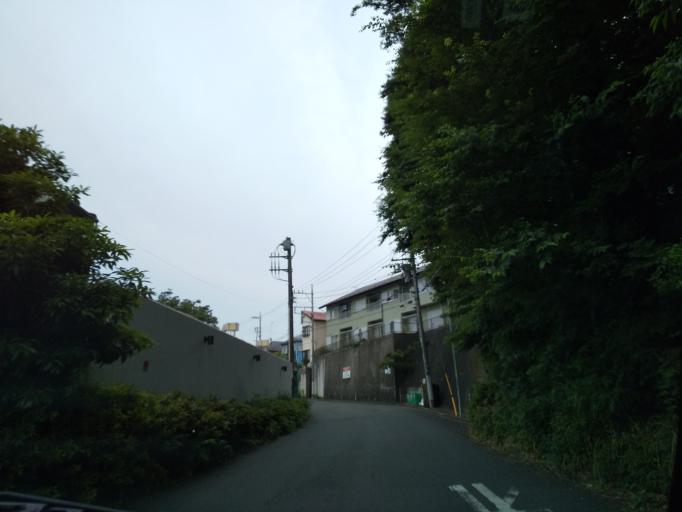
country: JP
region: Kanagawa
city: Atsugi
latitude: 35.4762
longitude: 139.3519
